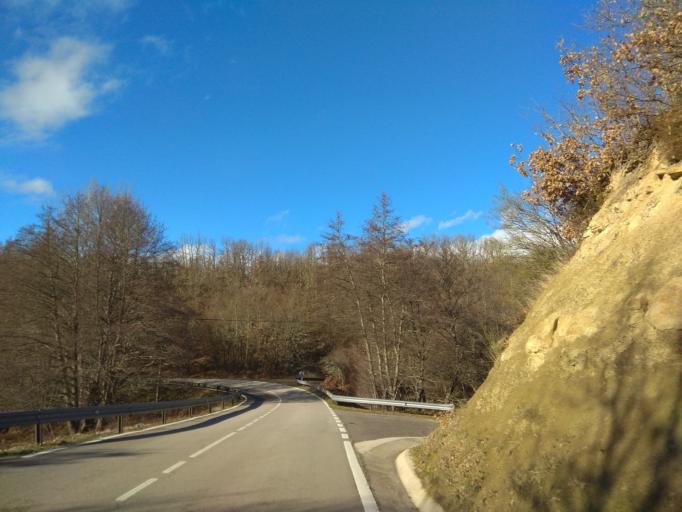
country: ES
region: Cantabria
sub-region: Provincia de Cantabria
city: San Martin de Elines
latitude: 42.9014
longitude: -3.8762
